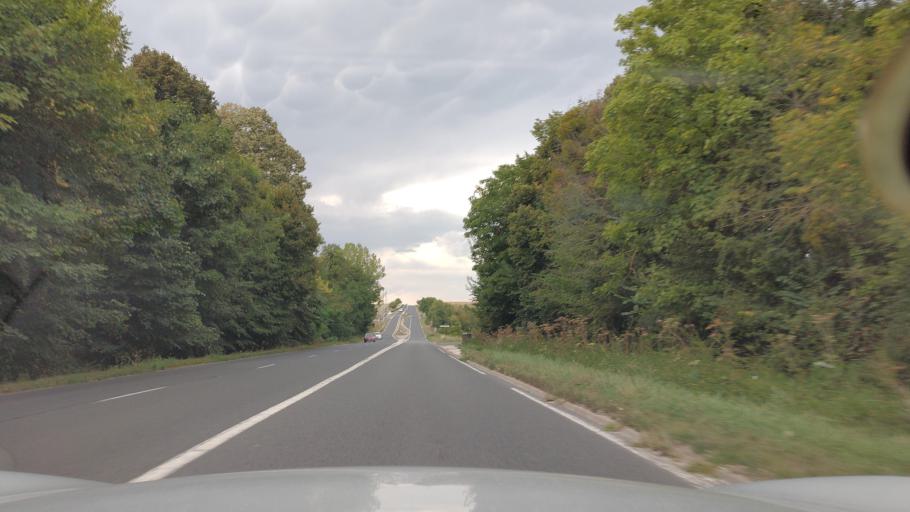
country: FR
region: Ile-de-France
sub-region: Departement de Seine-et-Marne
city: Grisy-Suisnes
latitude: 48.6806
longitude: 2.6490
